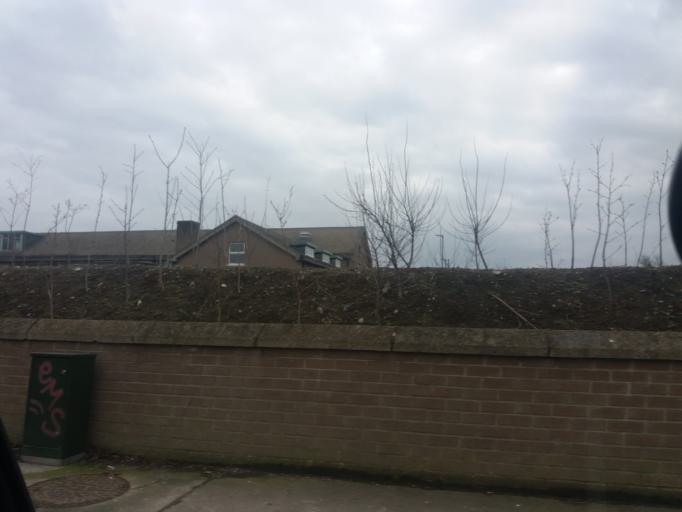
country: IE
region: Leinster
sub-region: Fingal County
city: Baldoyle
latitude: 53.3960
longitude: -6.1308
